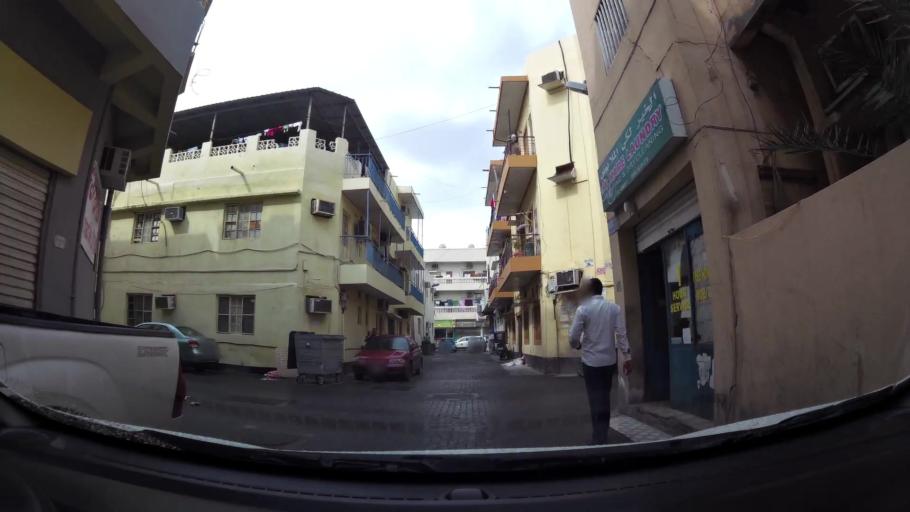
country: BH
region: Manama
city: Manama
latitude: 26.2327
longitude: 50.5925
